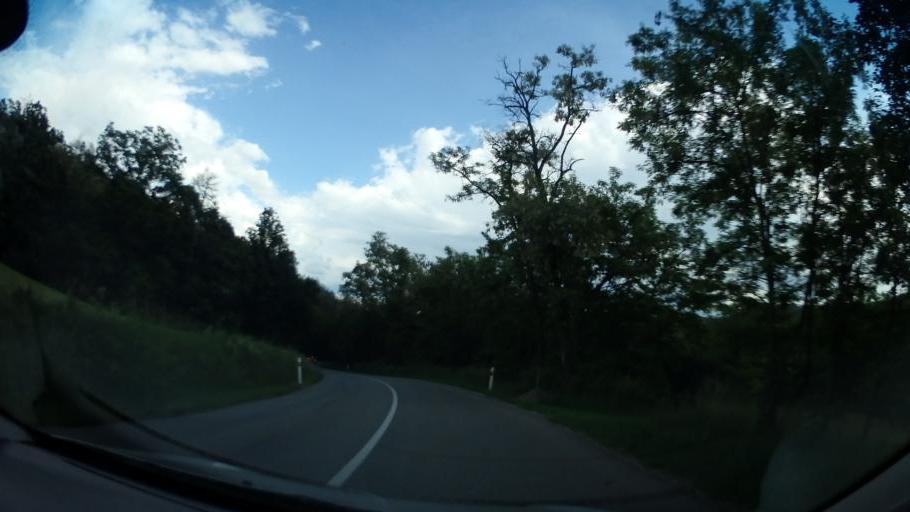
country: CZ
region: South Moravian
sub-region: Okres Brno-Venkov
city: Dolni Loucky
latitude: 49.3667
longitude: 16.3747
